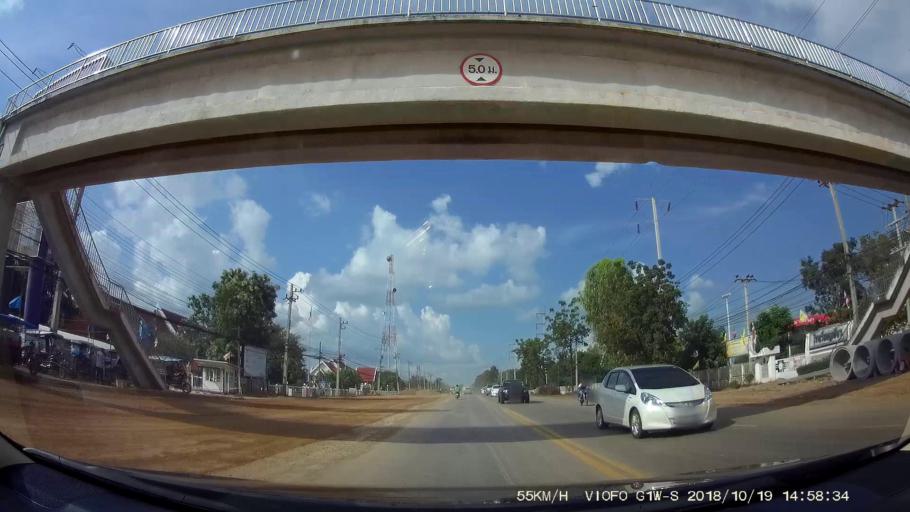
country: TH
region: Chaiyaphum
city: Phu Khiao
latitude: 16.3760
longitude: 102.1293
